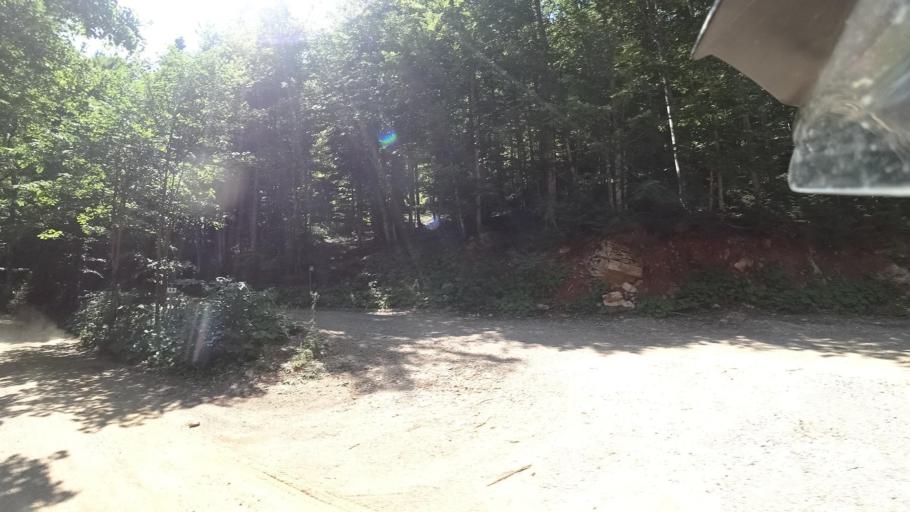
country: HR
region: Licko-Senjska
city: Popovaca
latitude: 44.5830
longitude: 15.1888
